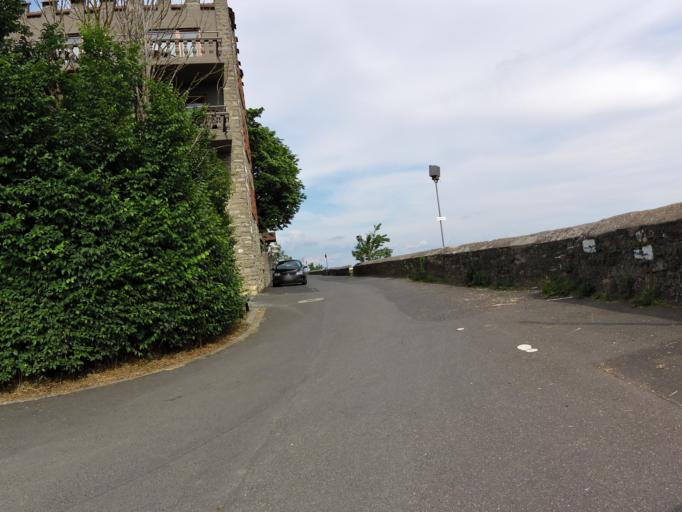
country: DE
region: Bavaria
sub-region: Regierungsbezirk Unterfranken
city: Hochberg
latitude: 49.8060
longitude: 9.9132
